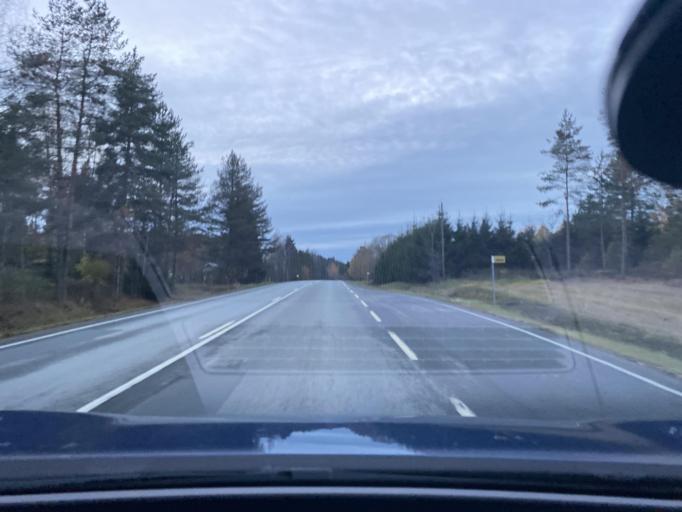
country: FI
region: Uusimaa
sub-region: Helsinki
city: Saukkola
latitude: 60.3847
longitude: 23.8897
